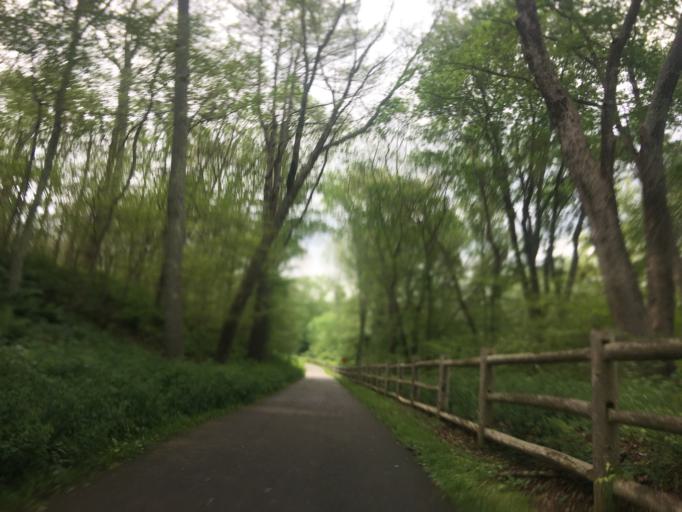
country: US
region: Connecticut
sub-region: Windham County
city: East Brooklyn
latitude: 41.7819
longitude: -71.8948
